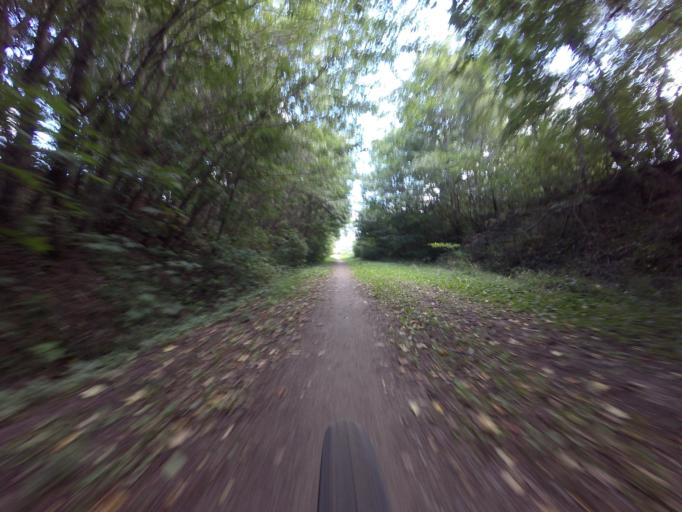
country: DK
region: South Denmark
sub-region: Vejle Kommune
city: Give
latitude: 55.9810
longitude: 9.2813
